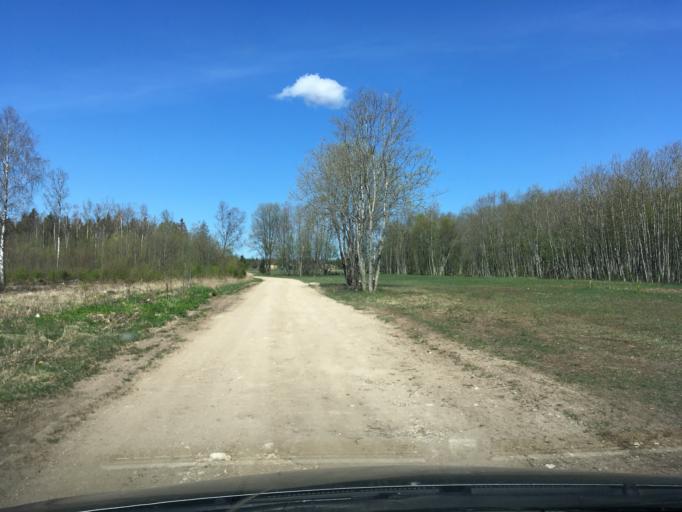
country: EE
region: Harju
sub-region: Raasiku vald
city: Raasiku
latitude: 59.2187
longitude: 25.1557
